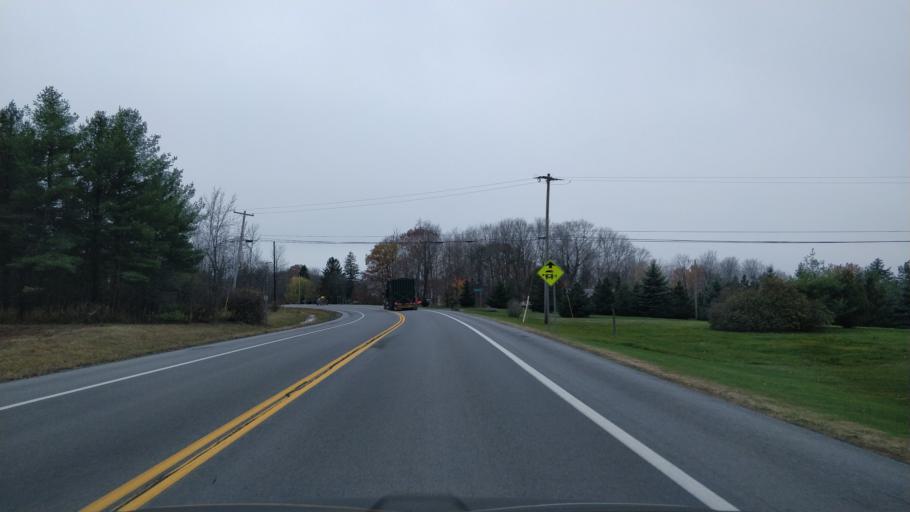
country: CA
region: Ontario
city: Brockville
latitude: 44.6035
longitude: -75.6212
